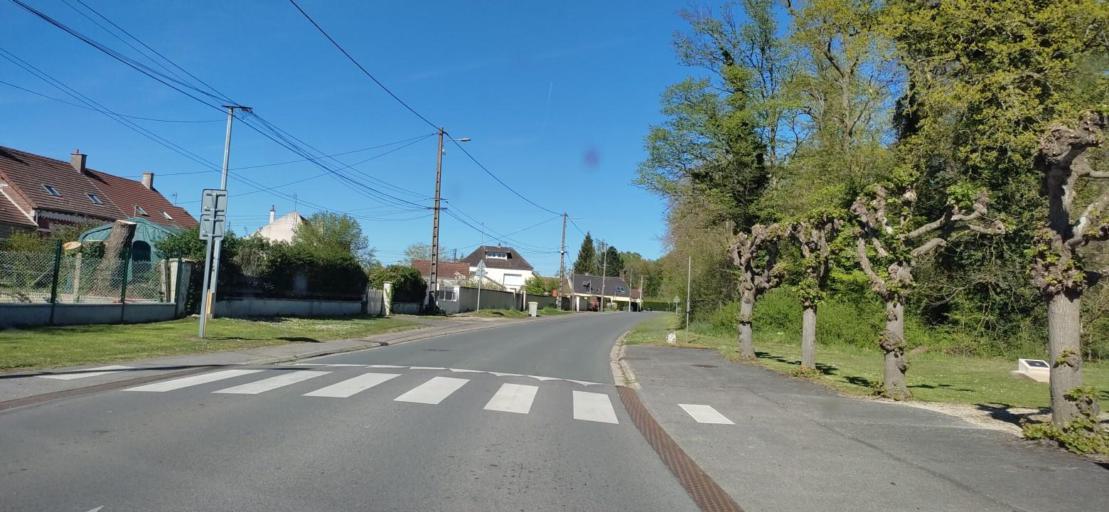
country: FR
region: Picardie
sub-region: Departement de l'Oise
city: Dreslincourt
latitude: 49.4837
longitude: 2.9560
